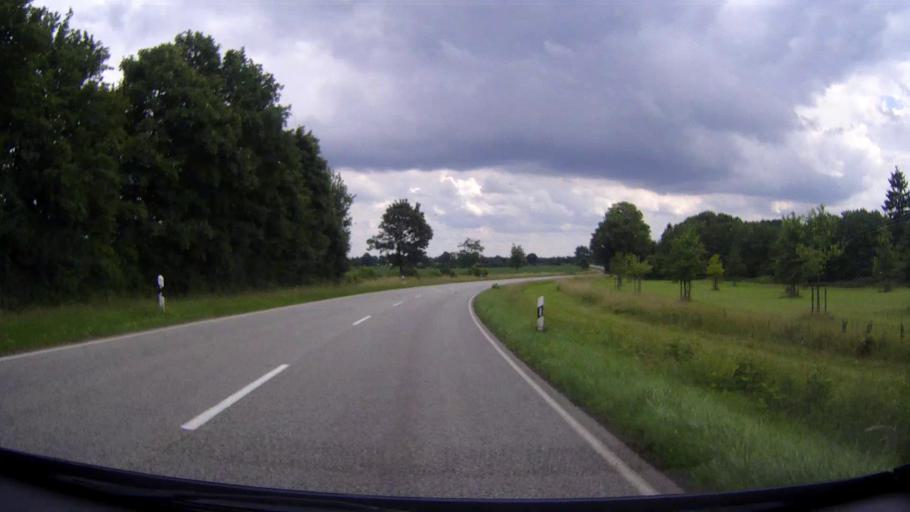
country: DE
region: Schleswig-Holstein
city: Warringholz
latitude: 54.0694
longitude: 9.4706
